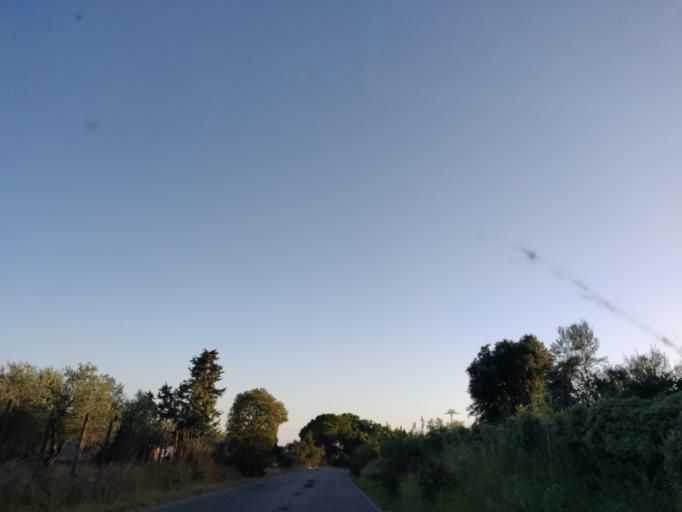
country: IT
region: Latium
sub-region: Provincia di Viterbo
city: Canino
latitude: 42.4169
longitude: 11.7040
